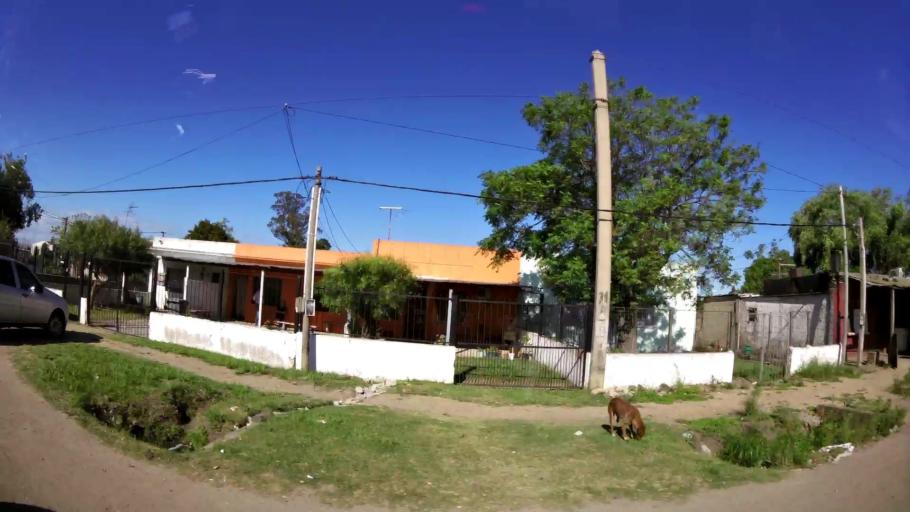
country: UY
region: Canelones
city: La Paz
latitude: -34.8185
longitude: -56.1569
